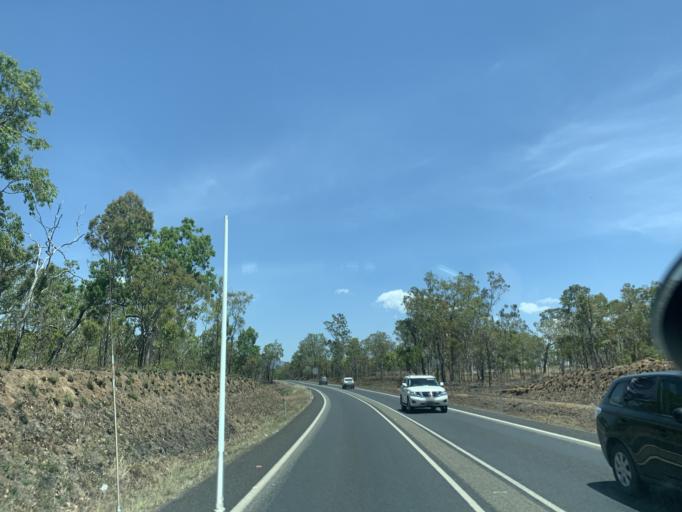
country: AU
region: Queensland
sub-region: Tablelands
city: Mareeba
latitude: -16.9480
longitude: 145.5383
